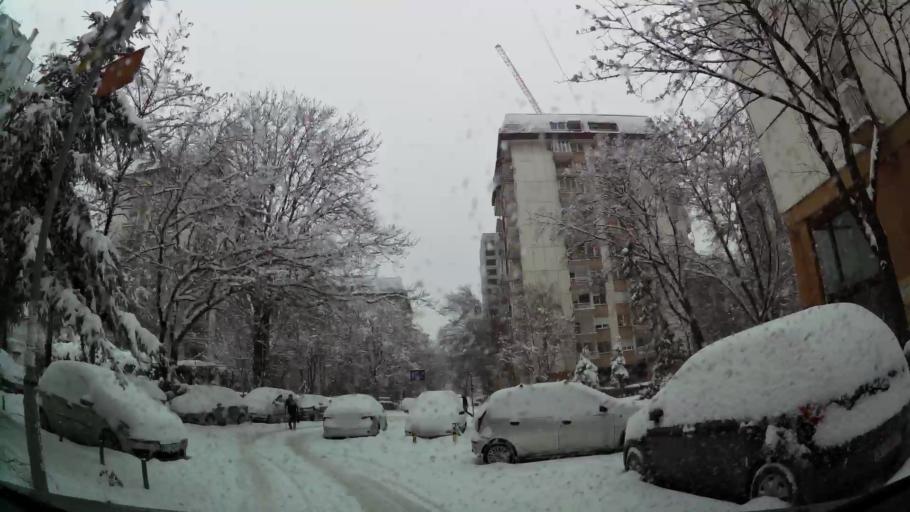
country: RS
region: Central Serbia
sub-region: Belgrade
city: Stari Grad
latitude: 44.8262
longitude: 20.4623
